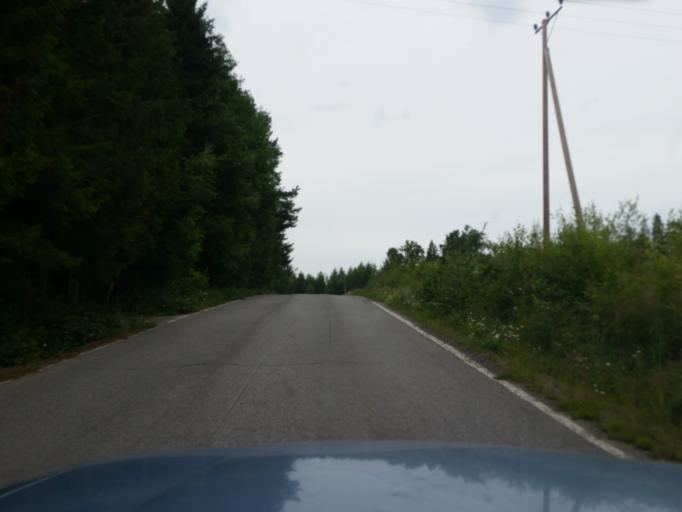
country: FI
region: Uusimaa
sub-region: Helsinki
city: Sammatti
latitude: 60.4667
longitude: 23.8454
